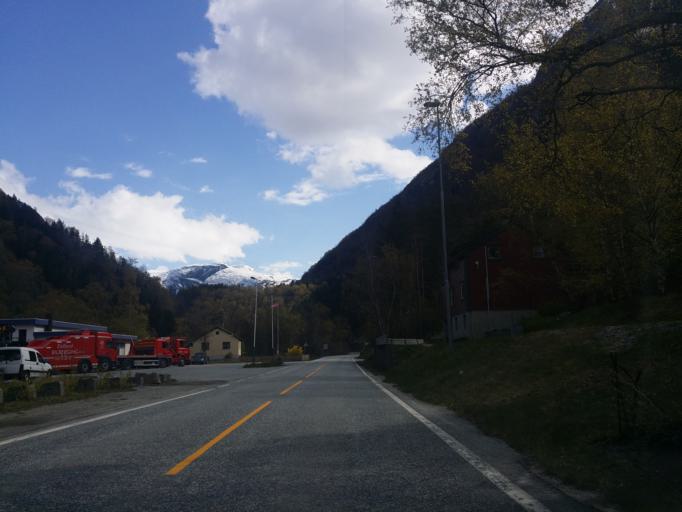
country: NO
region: Hordaland
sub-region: Eidfjord
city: Eidfjord
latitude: 60.4610
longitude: 7.0800
